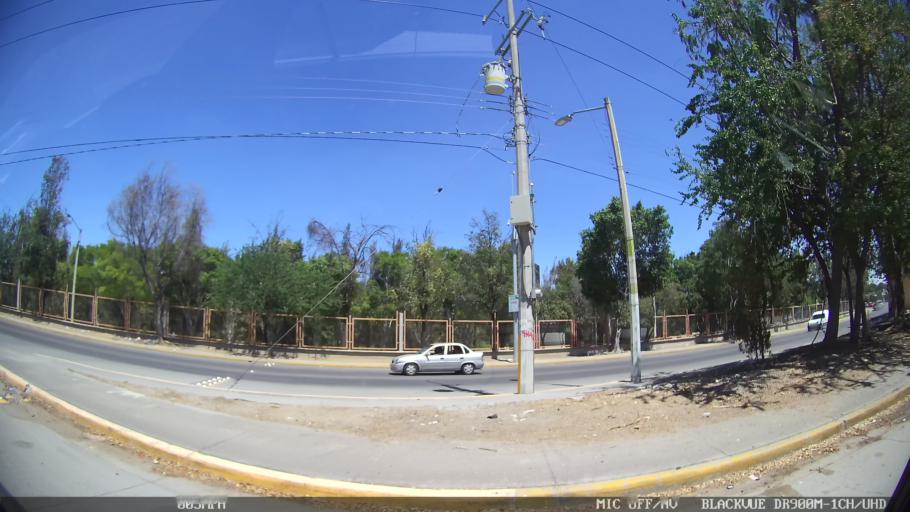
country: MX
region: Jalisco
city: Tlaquepaque
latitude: 20.6732
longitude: -103.2697
